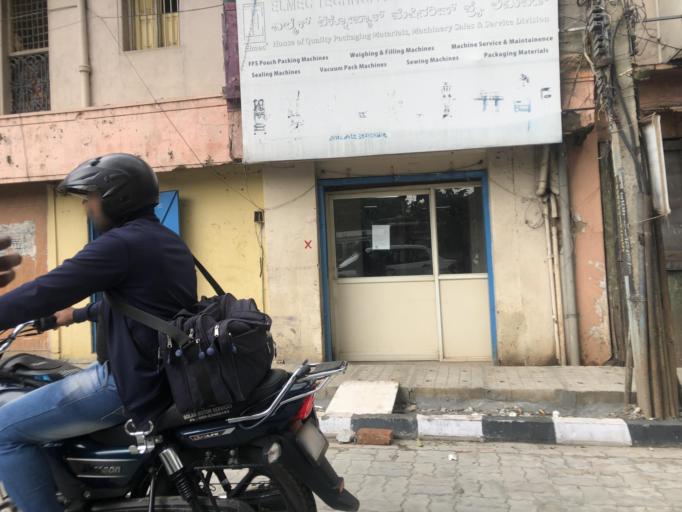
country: IN
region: Karnataka
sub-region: Bangalore Urban
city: Bangalore
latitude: 12.9711
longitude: 77.5684
